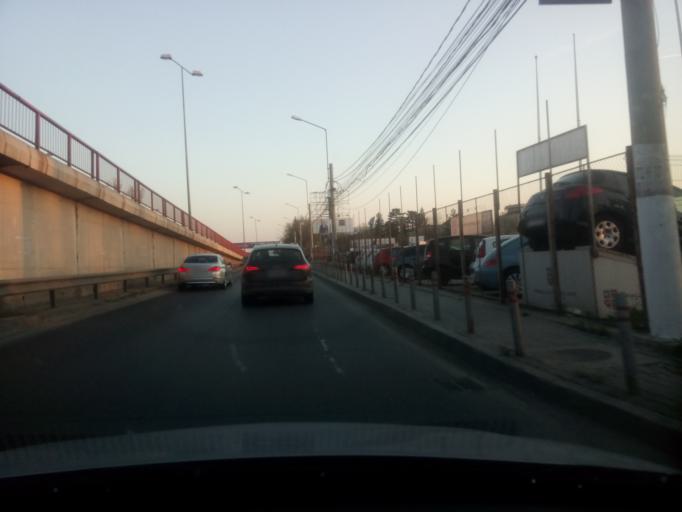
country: RO
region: Ilfov
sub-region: Comuna Otopeni
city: Otopeni
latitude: 44.5716
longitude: 26.0700
